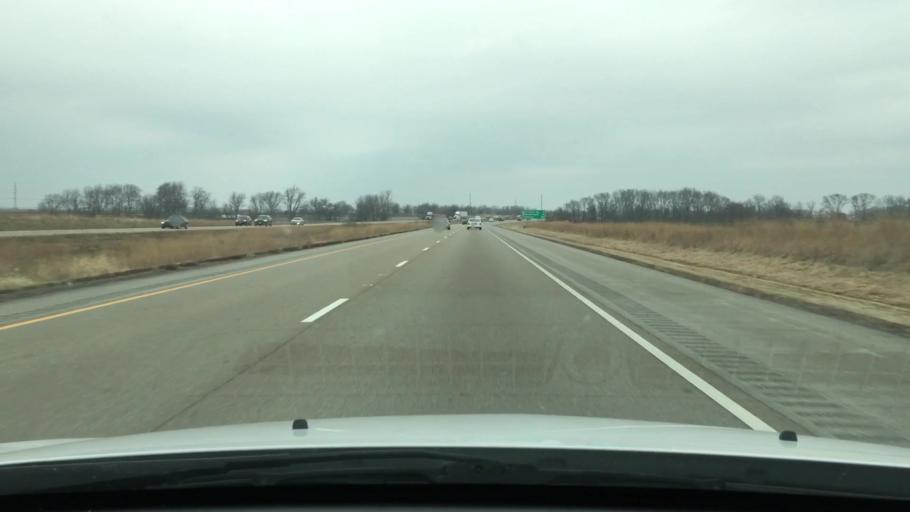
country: US
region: Illinois
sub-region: Logan County
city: Atlanta
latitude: 40.2707
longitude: -89.2127
